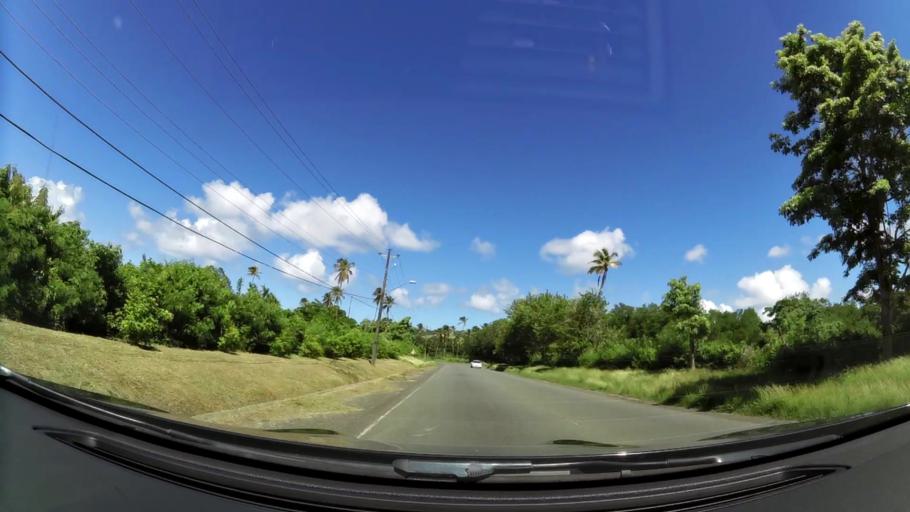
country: TT
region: Tobago
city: Scarborough
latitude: 11.1667
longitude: -60.7719
